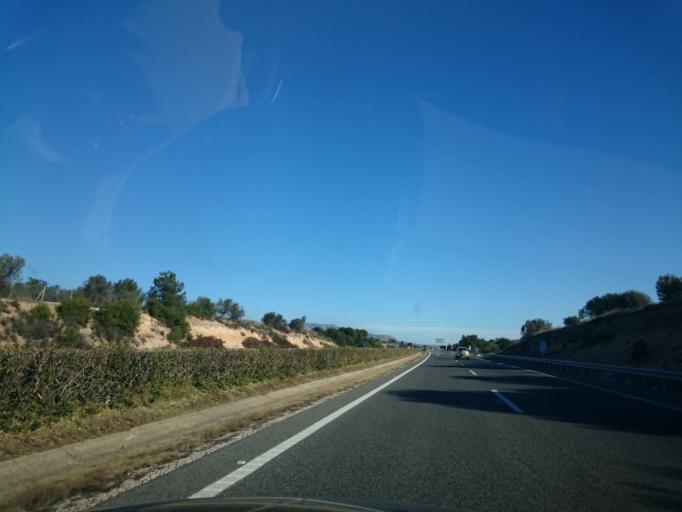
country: ES
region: Catalonia
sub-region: Provincia de Tarragona
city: l'Ametlla de Mar
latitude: 40.8781
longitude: 0.7910
